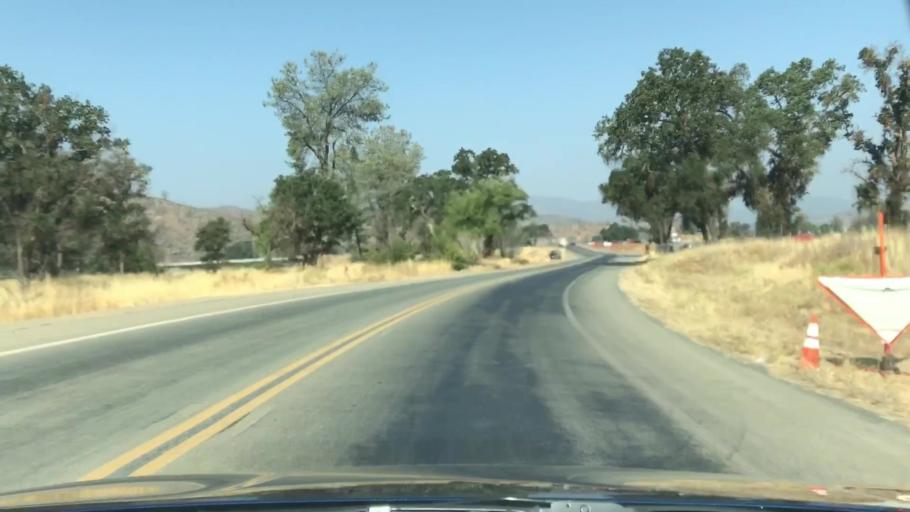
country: US
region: California
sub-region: Lake County
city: Hidden Valley Lake
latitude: 38.7912
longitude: -122.5620
